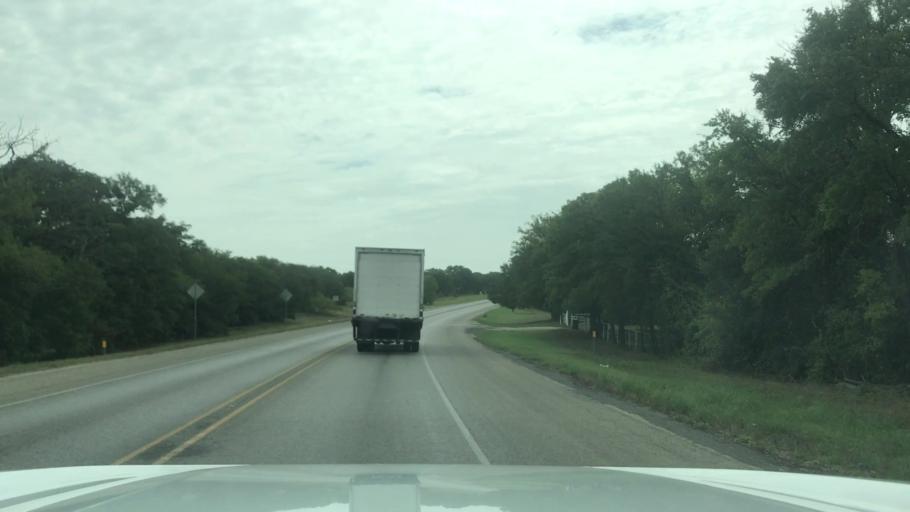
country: US
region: Texas
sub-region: Comanche County
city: De Leon
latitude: 32.1079
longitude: -98.4931
